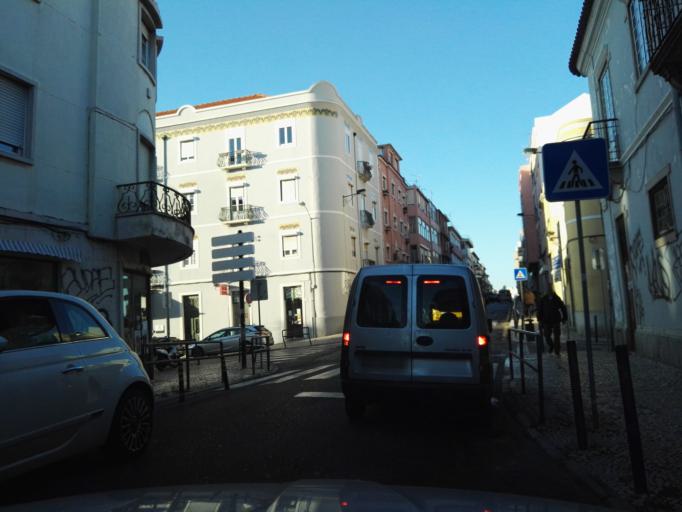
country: PT
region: Lisbon
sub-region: Lisbon
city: Lisbon
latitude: 38.7261
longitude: -9.1649
